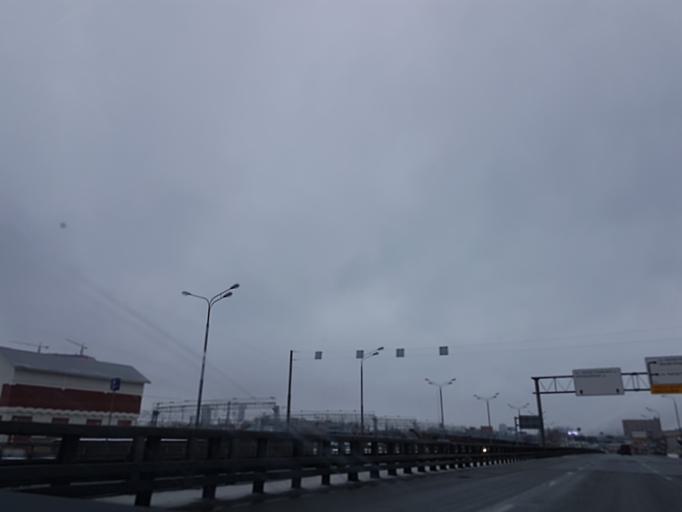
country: RU
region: Moskovskaya
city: Presnenskiy
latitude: 55.7623
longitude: 37.5226
